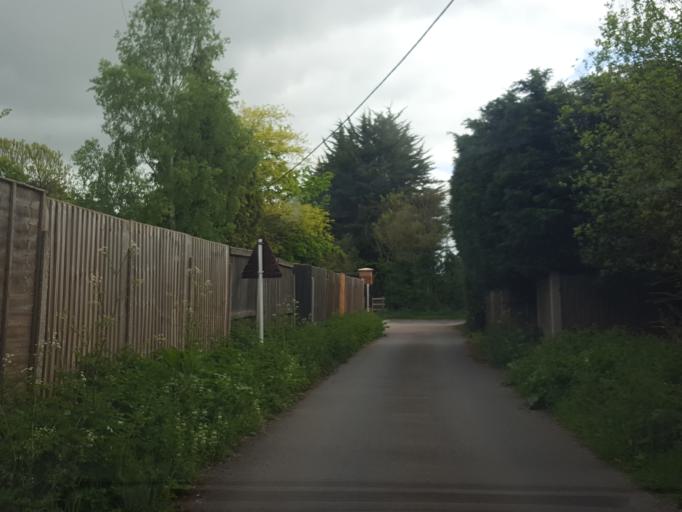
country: GB
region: England
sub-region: Essex
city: Alresford
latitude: 51.8435
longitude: 1.0230
